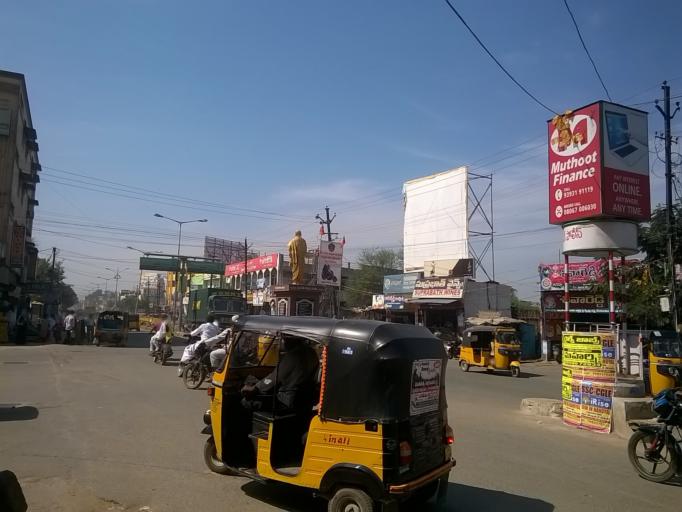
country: IN
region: Andhra Pradesh
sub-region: Kurnool
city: Nandyal
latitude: 15.4879
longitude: 78.4780
